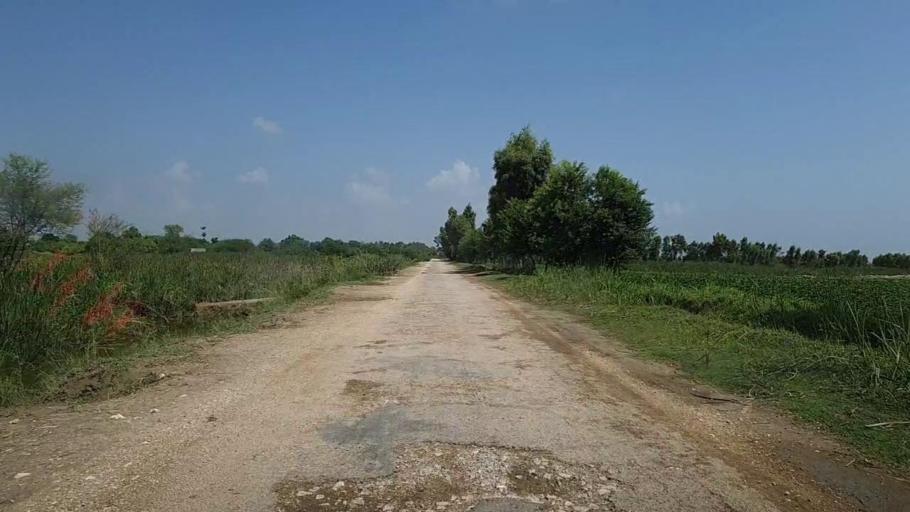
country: PK
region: Sindh
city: Bhiria
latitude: 26.8715
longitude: 68.2540
